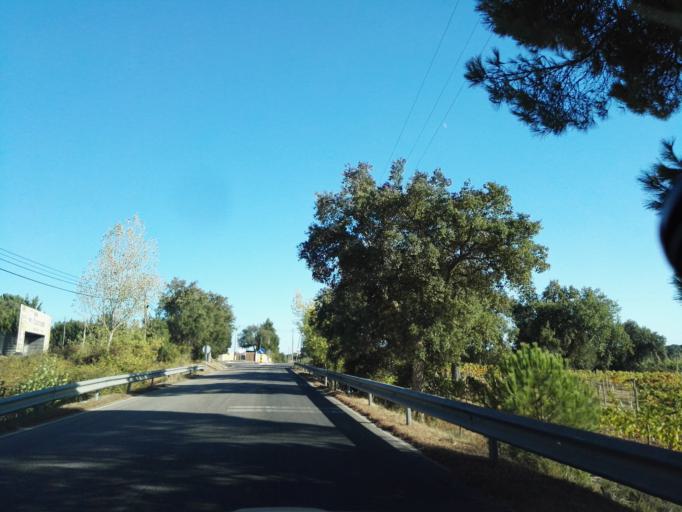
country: PT
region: Santarem
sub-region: Benavente
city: Poceirao
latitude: 38.8501
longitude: -8.7189
